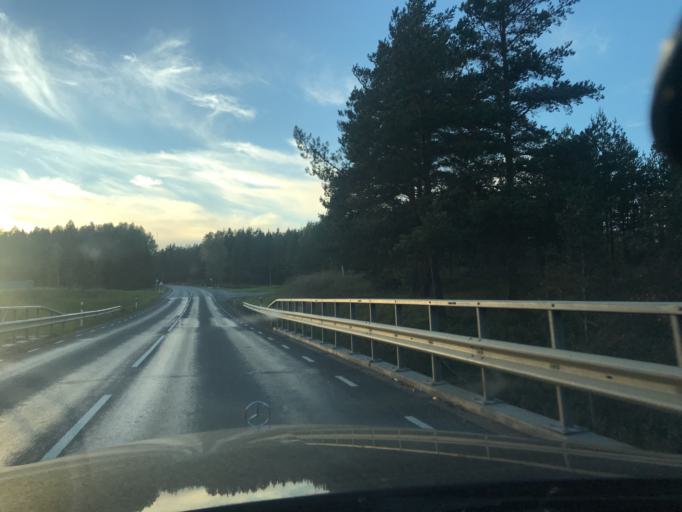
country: EE
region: Vorumaa
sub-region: Antsla vald
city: Vana-Antsla
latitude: 57.8828
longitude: 26.7389
